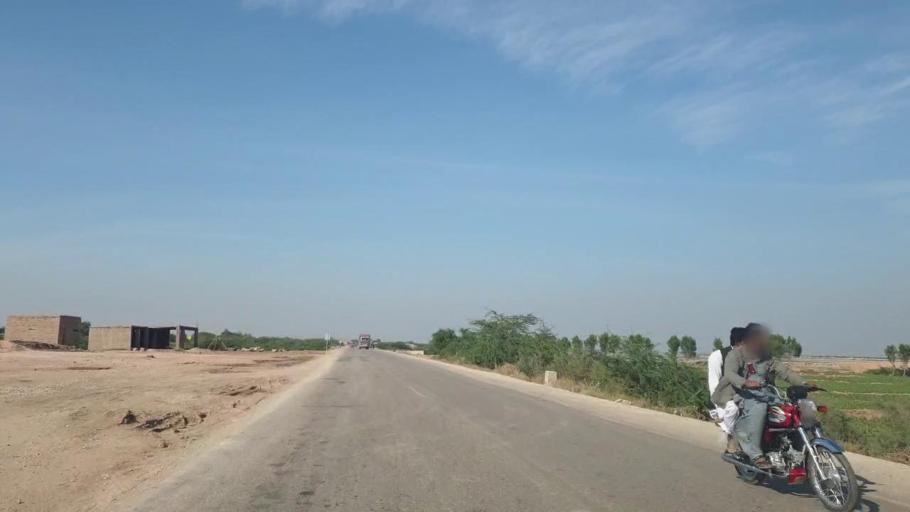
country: PK
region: Sindh
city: Sehwan
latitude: 26.3771
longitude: 67.8729
